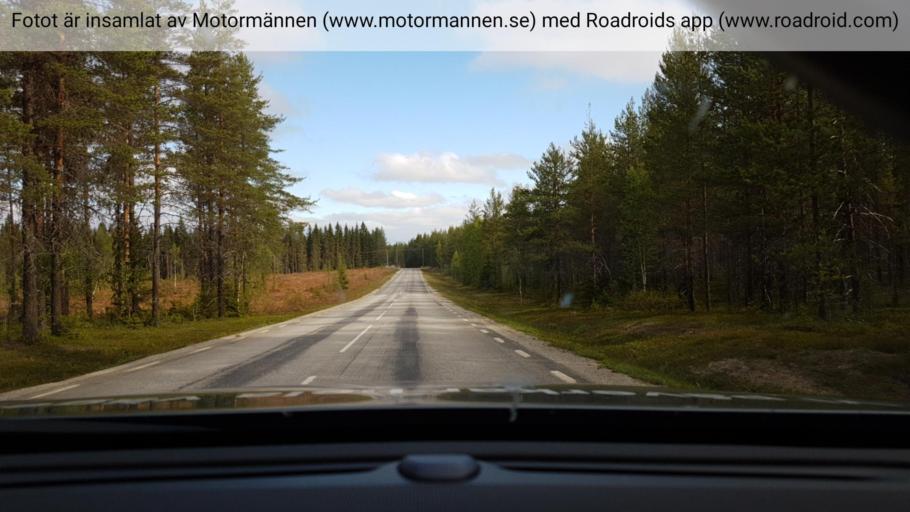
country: SE
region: Vaesterbotten
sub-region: Norsjo Kommun
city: Norsjoe
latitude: 64.7261
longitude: 19.1324
